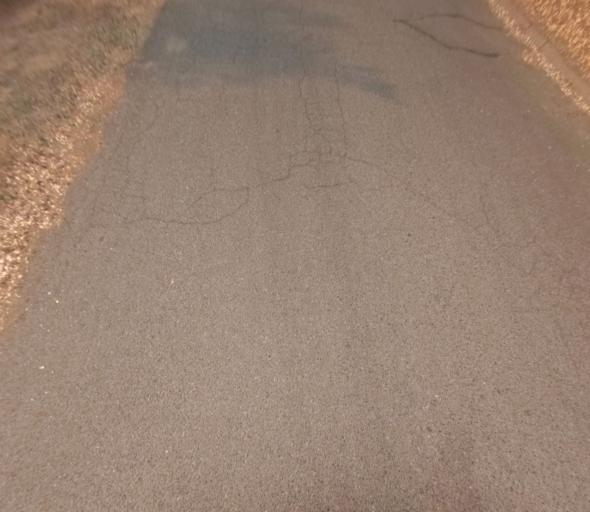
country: US
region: California
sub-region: Madera County
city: Oakhurst
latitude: 37.3220
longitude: -119.6297
